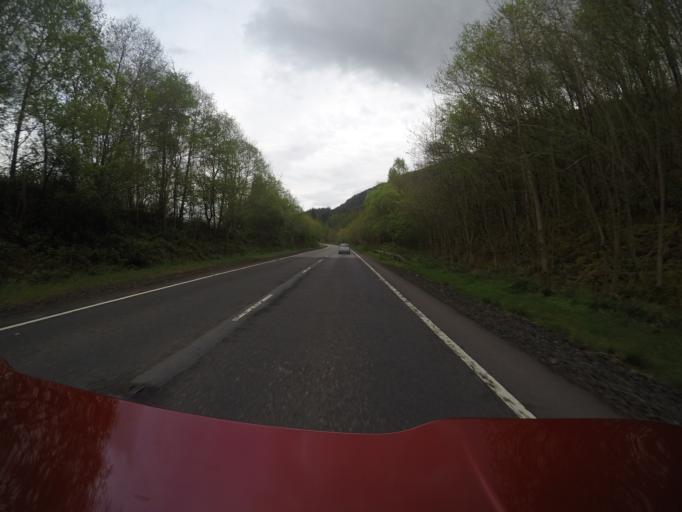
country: GB
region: Scotland
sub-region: Argyll and Bute
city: Helensburgh
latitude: 56.1221
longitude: -4.6518
